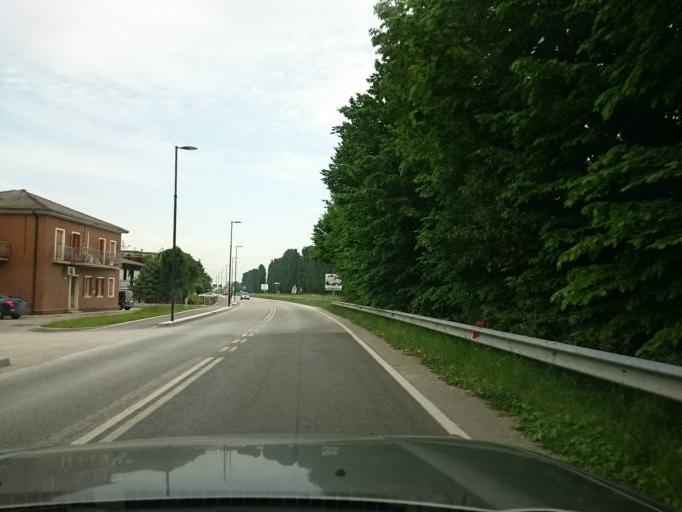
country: IT
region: Veneto
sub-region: Provincia di Venezia
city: Fornase
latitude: 45.4483
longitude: 12.1959
